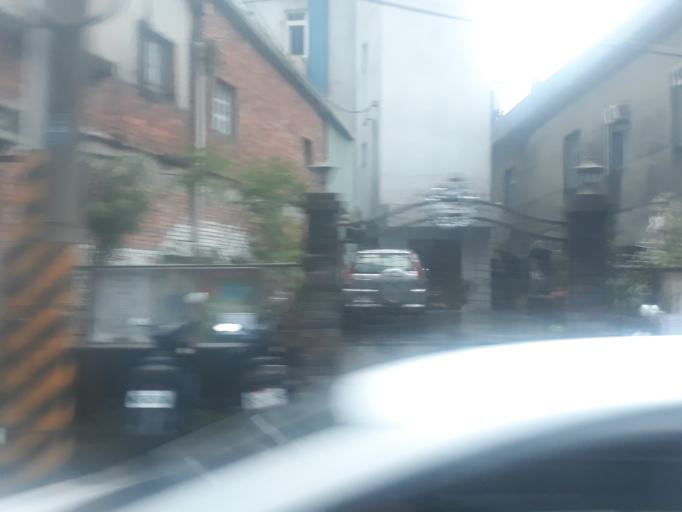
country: TW
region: Taipei
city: Taipei
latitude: 24.9877
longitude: 121.5704
